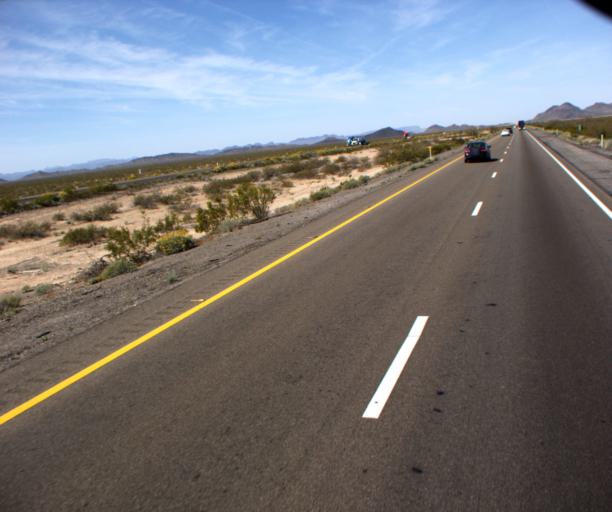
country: US
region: Arizona
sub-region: La Paz County
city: Salome
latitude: 33.5990
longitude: -113.5503
